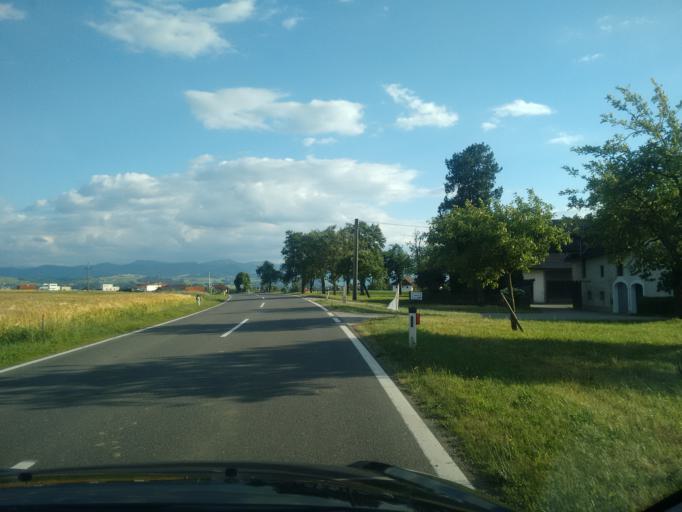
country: AT
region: Upper Austria
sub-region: Politischer Bezirk Steyr-Land
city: Sierning
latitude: 48.0573
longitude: 14.3151
